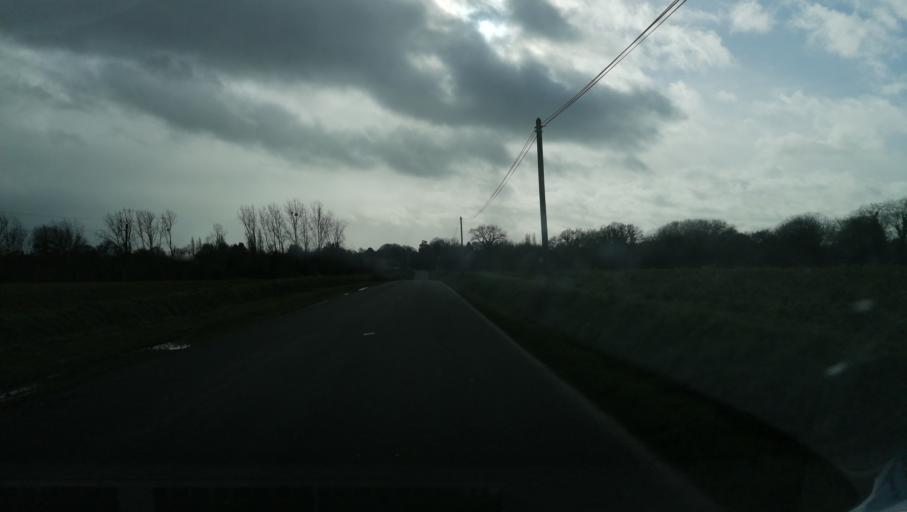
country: FR
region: Brittany
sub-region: Departement des Cotes-d'Armor
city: Lantic
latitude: 48.5857
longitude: -2.9161
